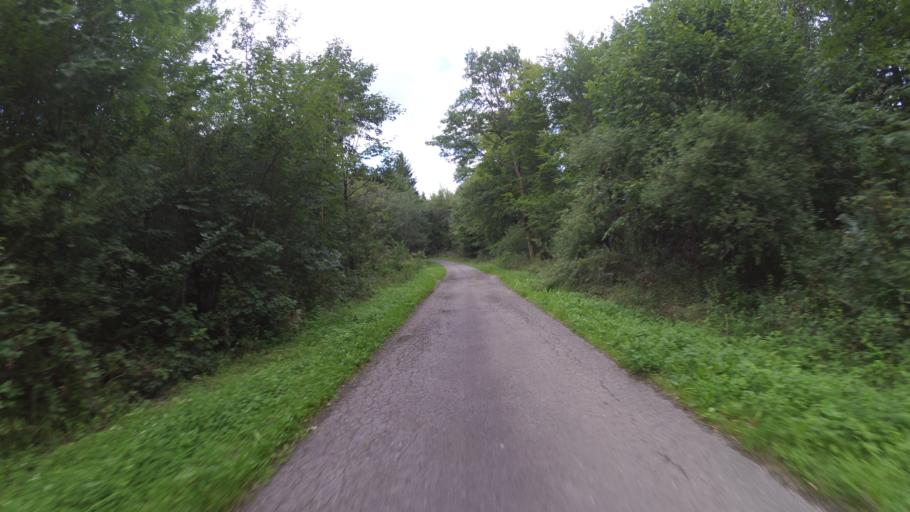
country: DE
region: Saarland
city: Nonnweiler
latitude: 49.5889
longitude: 6.9838
